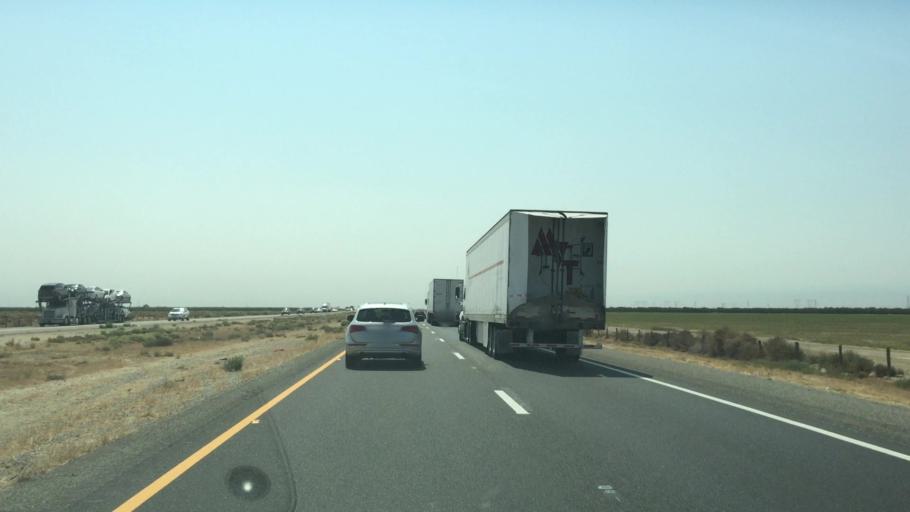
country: US
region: California
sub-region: Kern County
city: Buttonwillow
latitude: 35.3752
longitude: -119.3649
